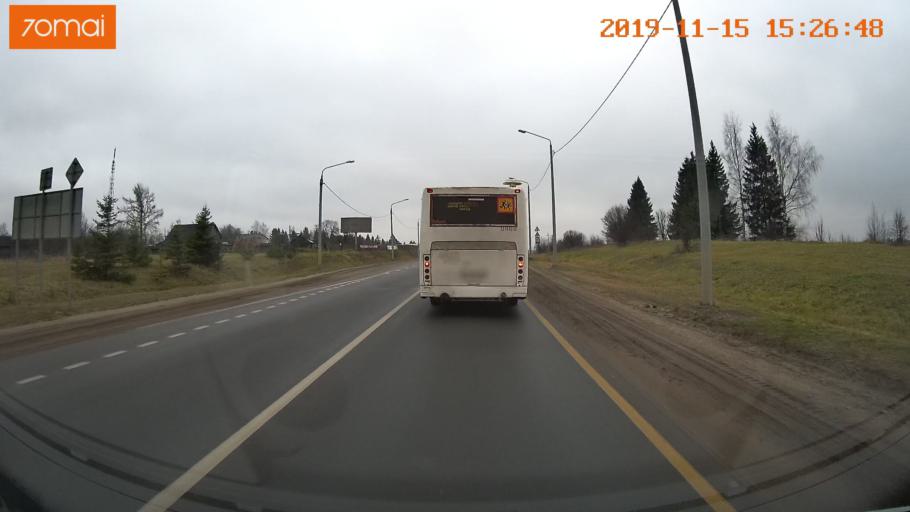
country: RU
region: Jaroslavl
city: Danilov
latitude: 58.1478
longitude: 40.1480
